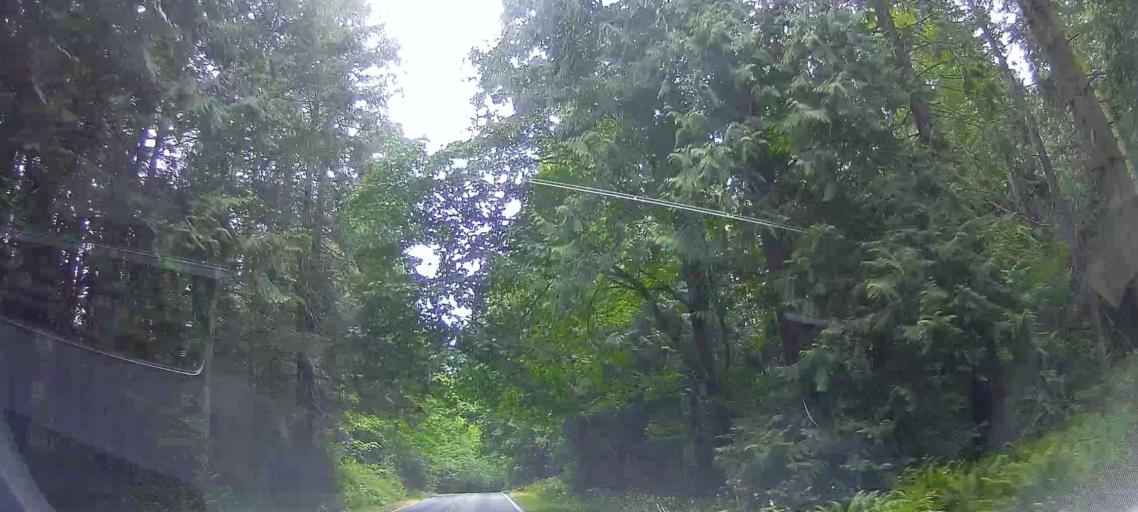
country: US
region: Washington
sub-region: Skagit County
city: Anacortes
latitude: 48.4771
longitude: -122.6268
